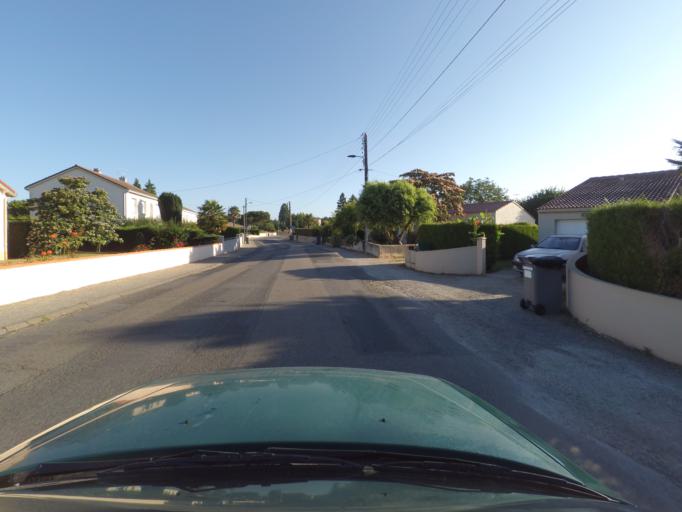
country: FR
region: Pays de la Loire
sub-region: Departement de la Loire-Atlantique
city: Montbert
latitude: 47.0590
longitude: -1.4830
